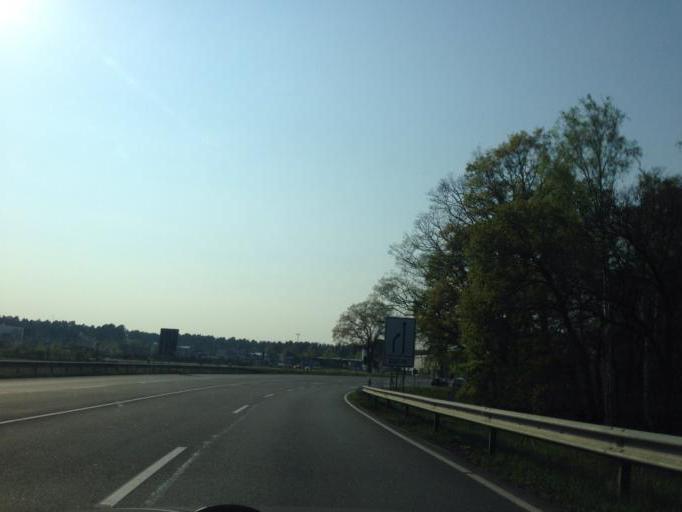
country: DE
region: Lower Saxony
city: Adelheidsdorf
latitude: 52.5841
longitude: 10.0686
